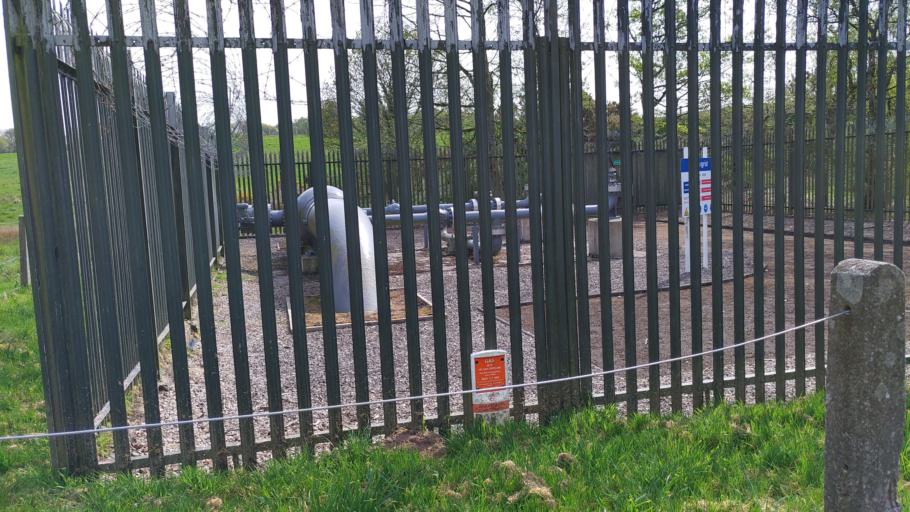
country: GB
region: England
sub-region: Lancashire
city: Chorley
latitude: 53.6689
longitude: -2.5983
